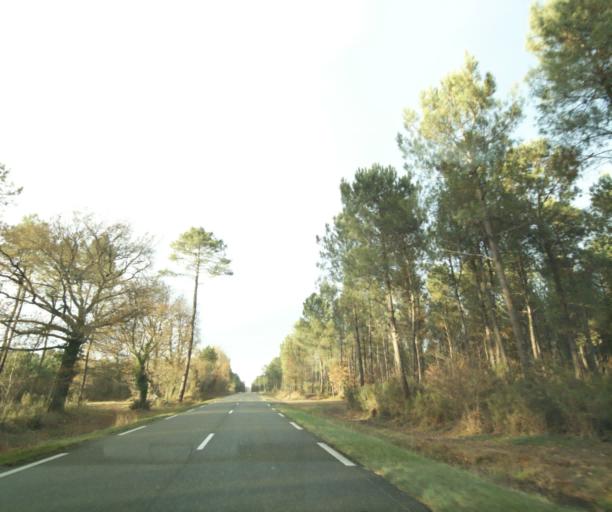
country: FR
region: Aquitaine
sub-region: Departement des Landes
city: Gabarret
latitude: 44.0383
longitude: -0.0341
